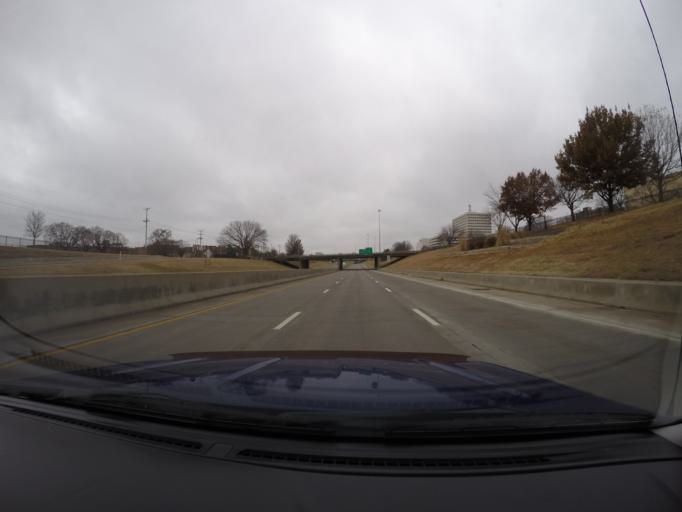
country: US
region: Kansas
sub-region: Shawnee County
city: Topeka
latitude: 39.0495
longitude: -95.6702
